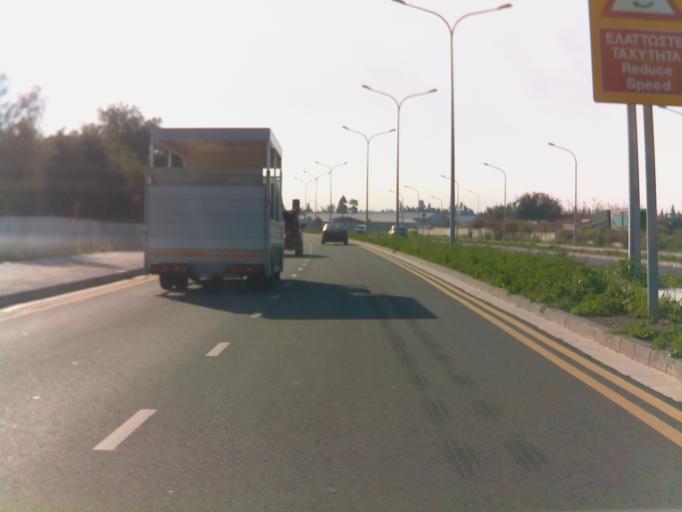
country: CY
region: Limassol
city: Ypsonas
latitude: 34.6674
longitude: 32.9900
